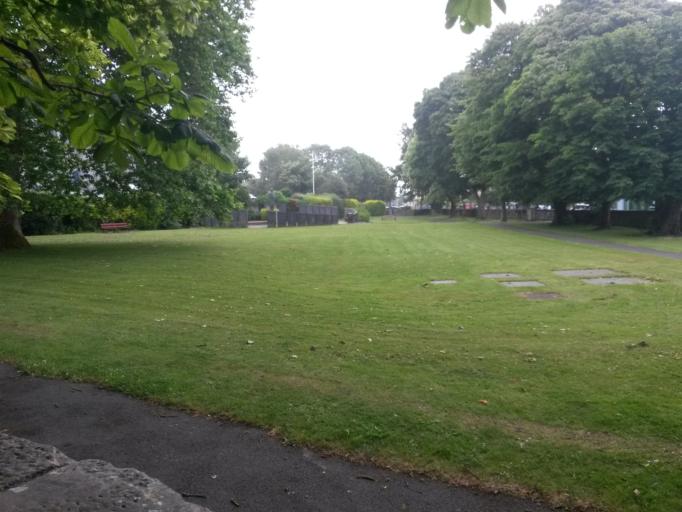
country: IE
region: Munster
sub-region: An Clar
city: Ennis
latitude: 52.8481
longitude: -8.9814
